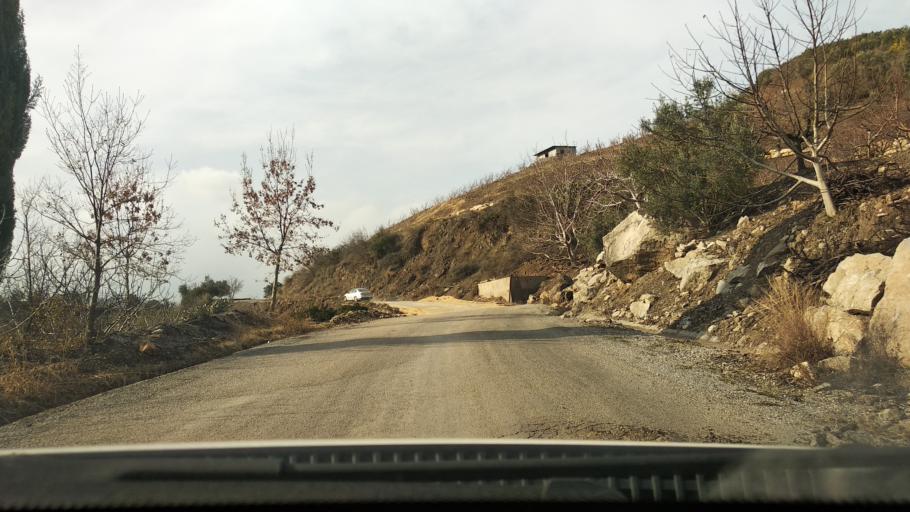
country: TR
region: Mersin
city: Kuzucubelen
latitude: 36.8693
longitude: 34.4704
